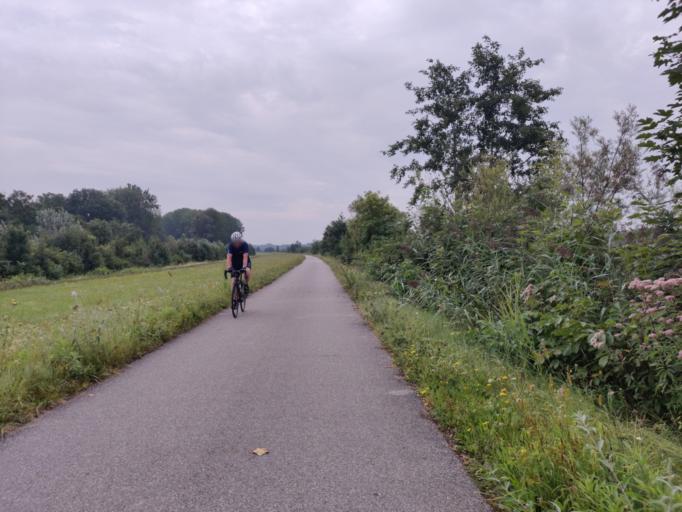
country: AT
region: Upper Austria
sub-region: Politischer Bezirk Urfahr-Umgebung
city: Steyregg
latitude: 48.2659
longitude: 14.3896
